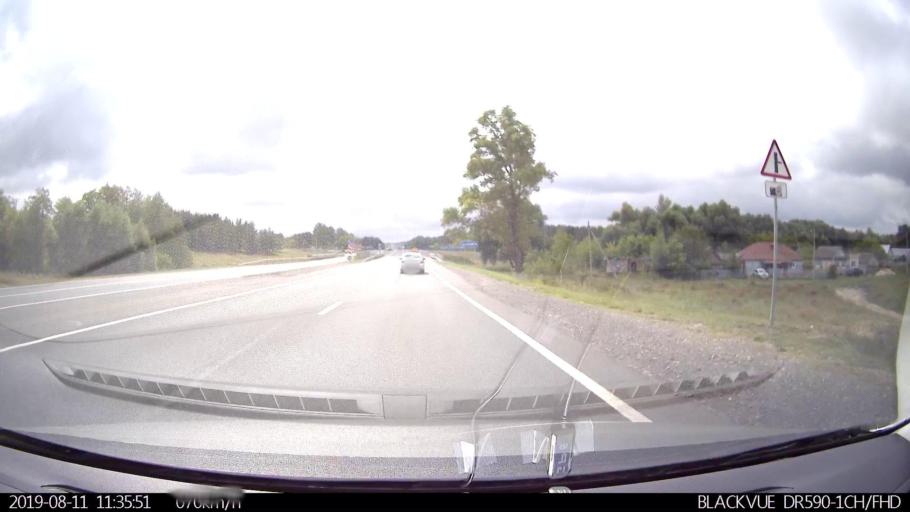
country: RU
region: Ulyanovsk
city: Silikatnyy
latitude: 54.0021
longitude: 48.2209
